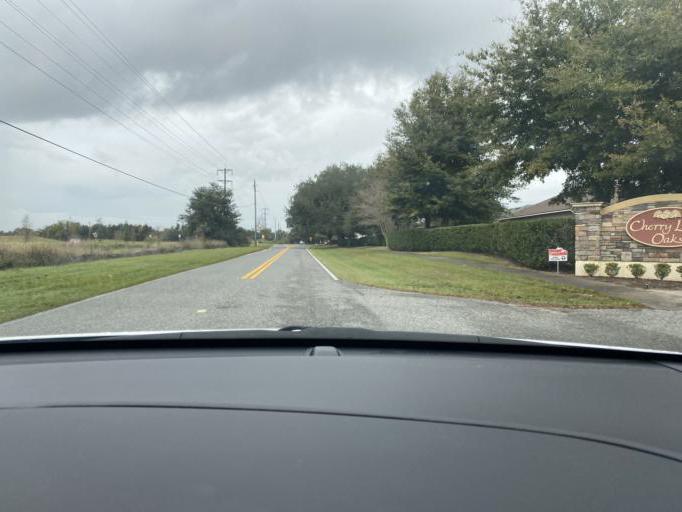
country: US
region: Florida
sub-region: Lake County
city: Minneola
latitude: 28.5947
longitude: -81.7835
